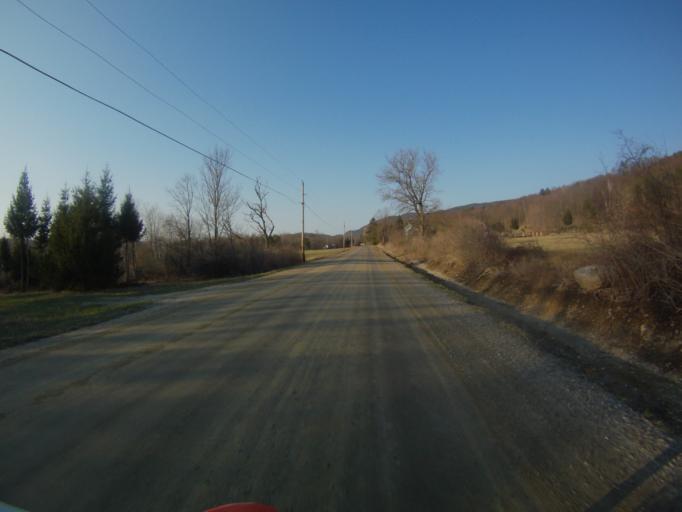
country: US
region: Vermont
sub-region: Addison County
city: Bristol
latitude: 44.1117
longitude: -73.0894
